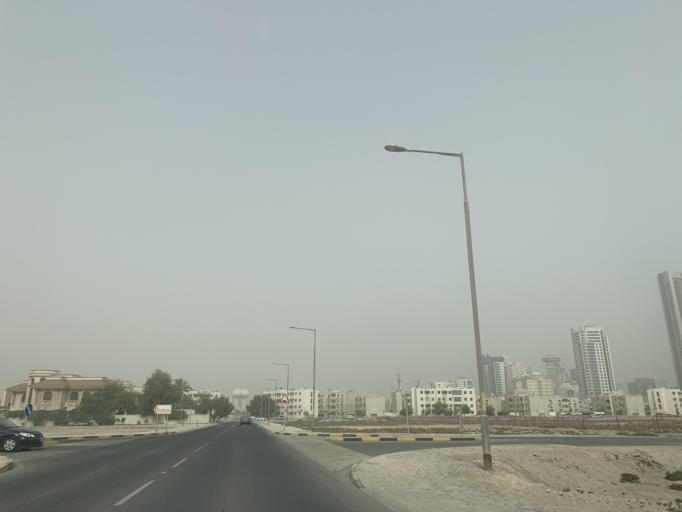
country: BH
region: Manama
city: Jidd Hafs
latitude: 26.2273
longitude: 50.5538
